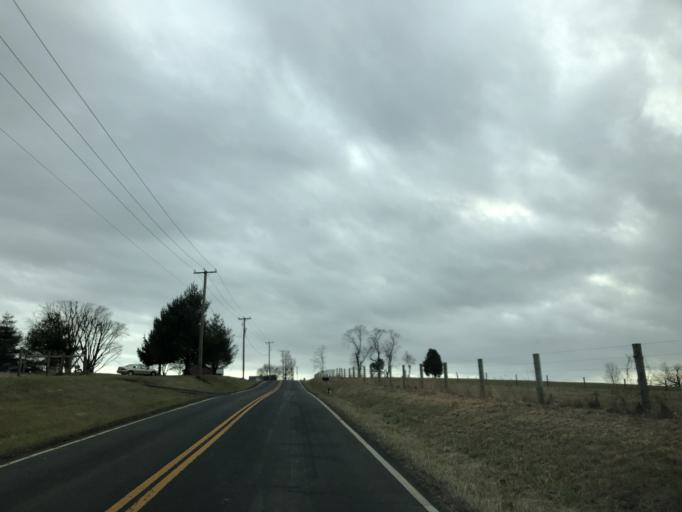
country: US
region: Maryland
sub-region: Cecil County
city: North East
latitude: 39.6806
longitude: -75.9518
